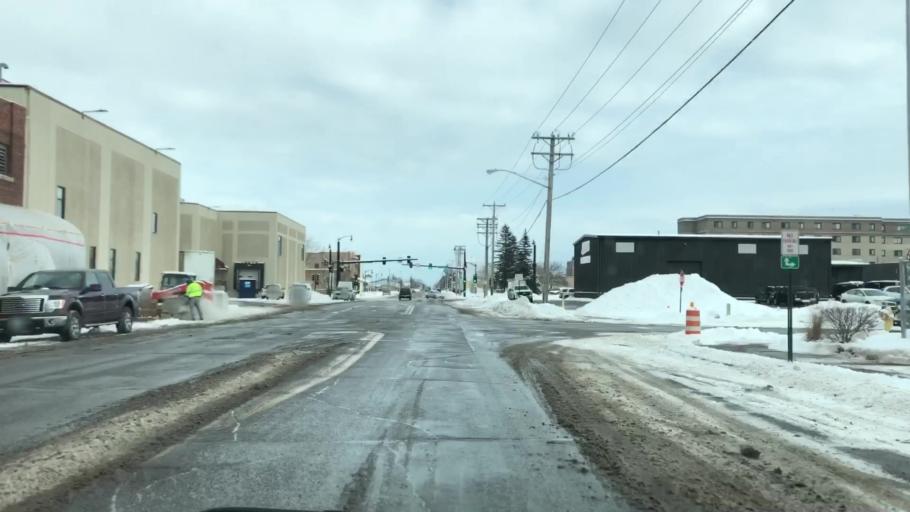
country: US
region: Wisconsin
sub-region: Douglas County
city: Superior
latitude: 46.7279
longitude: -92.1058
